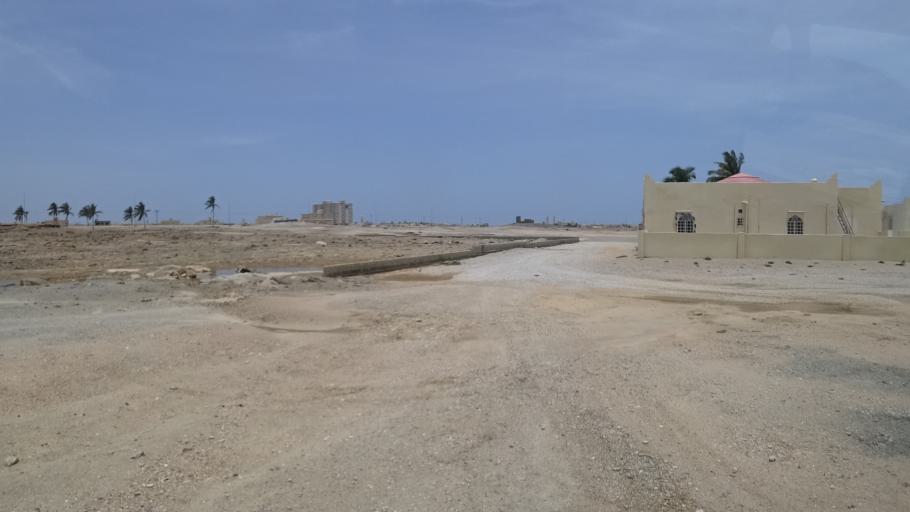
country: OM
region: Zufar
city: Salalah
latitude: 16.9998
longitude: 54.6940
